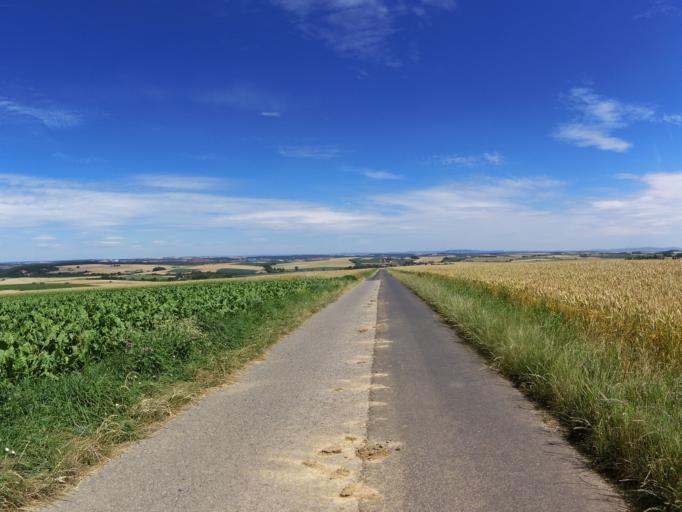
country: DE
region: Bavaria
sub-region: Regierungsbezirk Unterfranken
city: Geroldshausen
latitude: 49.7077
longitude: 9.8948
